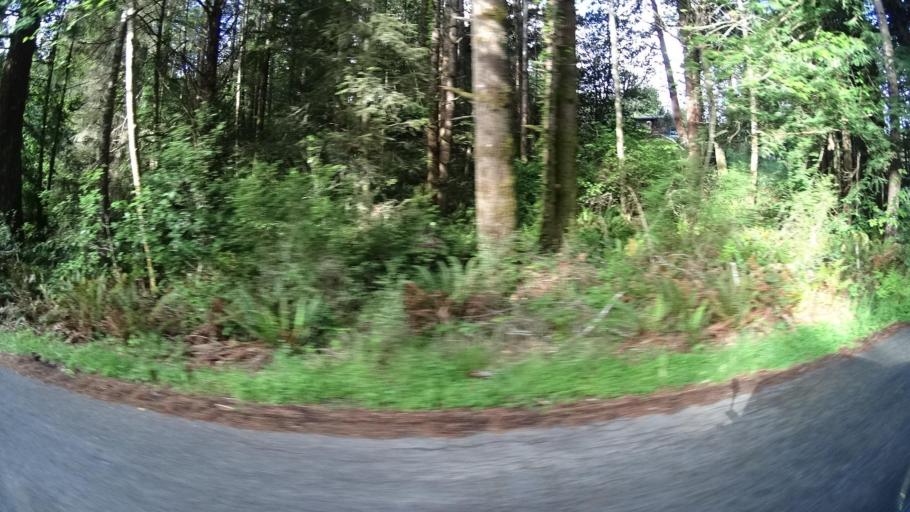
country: US
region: California
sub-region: Humboldt County
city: Blue Lake
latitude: 40.8832
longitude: -124.0238
